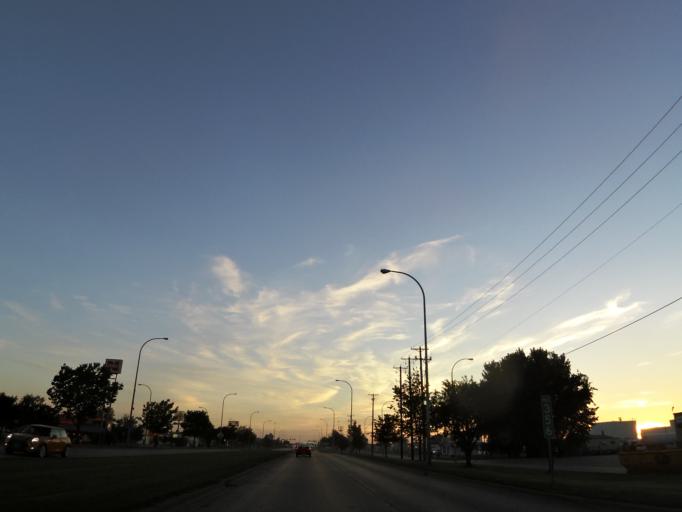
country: US
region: North Dakota
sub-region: Grand Forks County
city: Grand Forks
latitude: 47.9331
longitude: -97.0820
